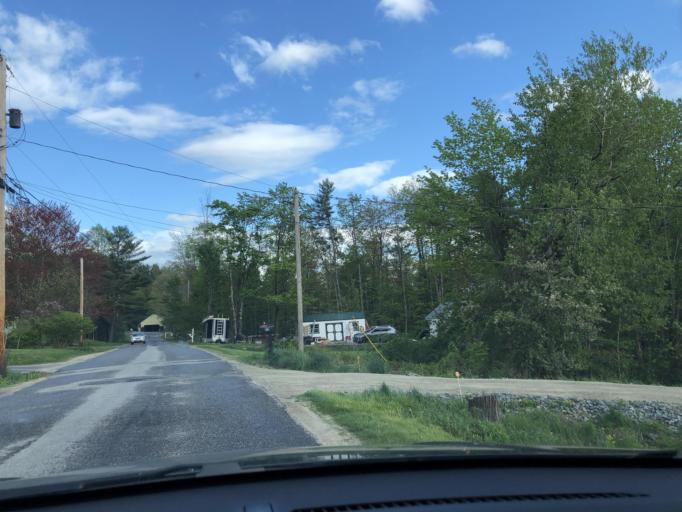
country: US
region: New Hampshire
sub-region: Merrimack County
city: New London
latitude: 43.4108
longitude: -71.9826
